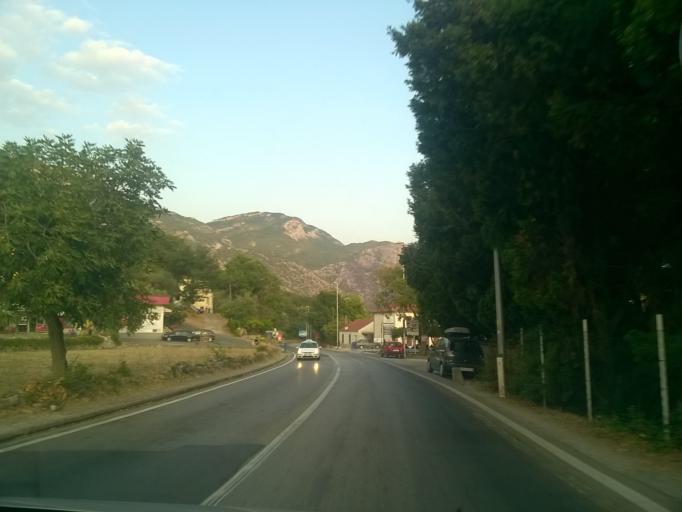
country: ME
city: Petrovac na Moru
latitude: 42.2000
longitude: 18.9648
